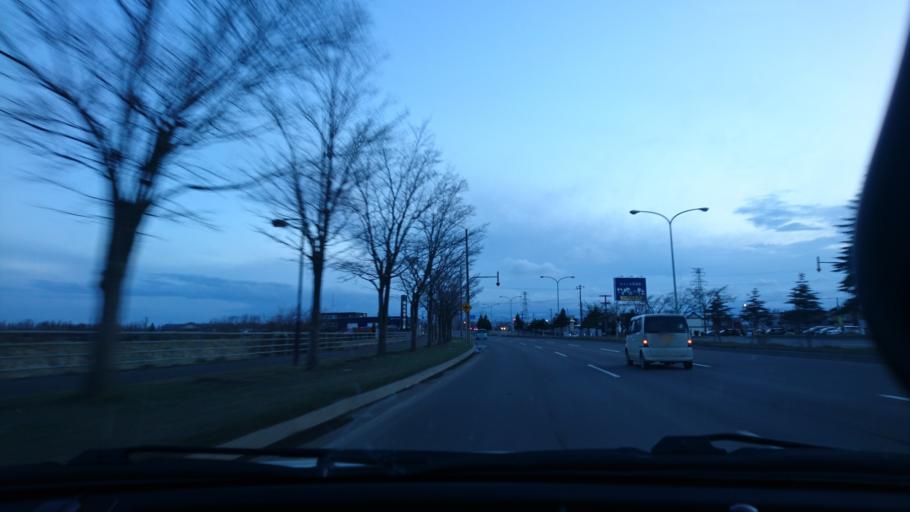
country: JP
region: Hokkaido
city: Sapporo
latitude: 43.1259
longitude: 141.4166
